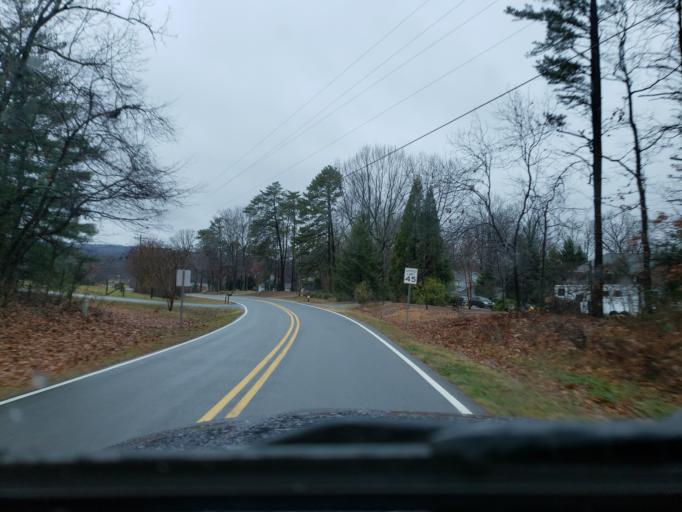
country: US
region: North Carolina
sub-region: Cleveland County
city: White Plains
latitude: 35.1755
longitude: -81.3633
